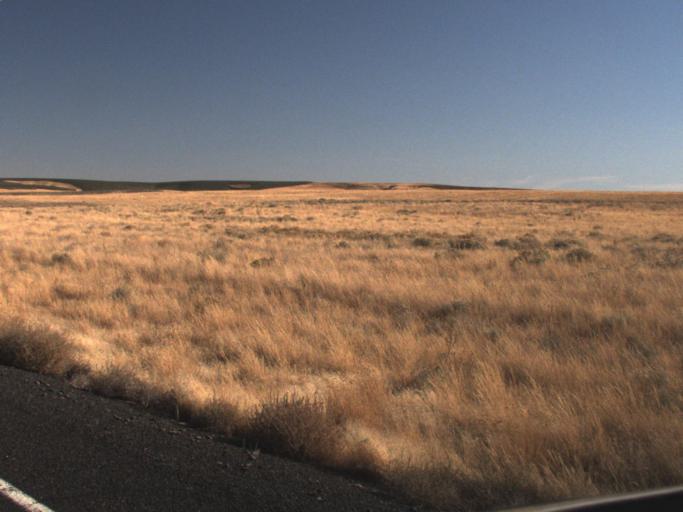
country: US
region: Washington
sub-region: Franklin County
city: Connell
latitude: 46.7108
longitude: -118.5394
